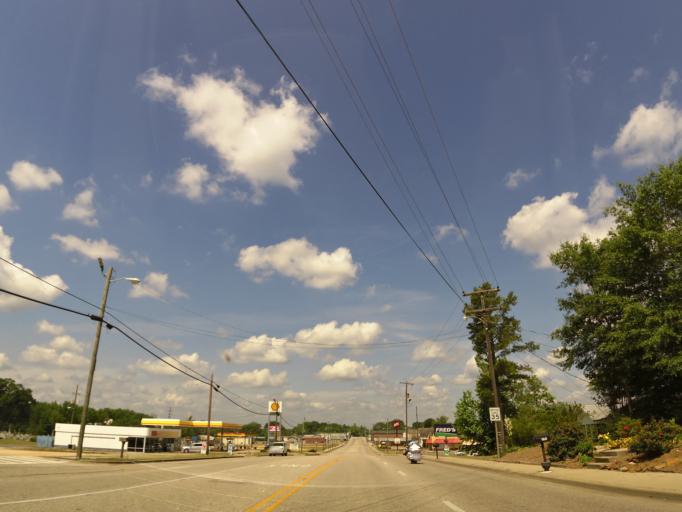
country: US
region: Alabama
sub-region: Marion County
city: Guin
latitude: 33.9661
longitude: -87.9088
